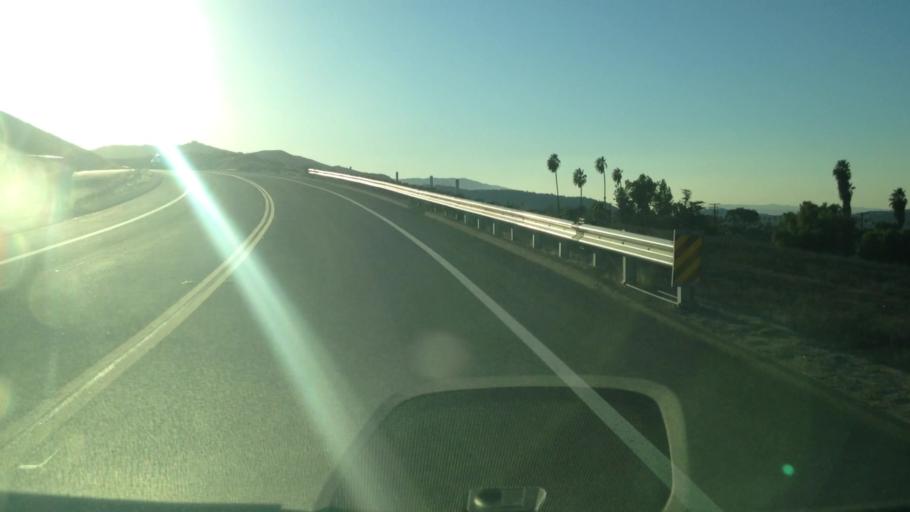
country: US
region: California
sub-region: Riverside County
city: Riverside
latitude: 33.8896
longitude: -117.4286
